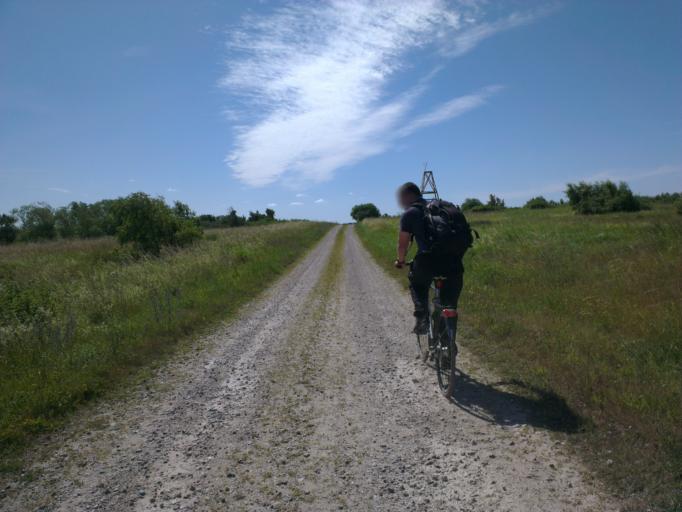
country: DK
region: Capital Region
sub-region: Frederikssund Kommune
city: Jaegerspris
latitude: 55.8791
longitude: 11.9384
